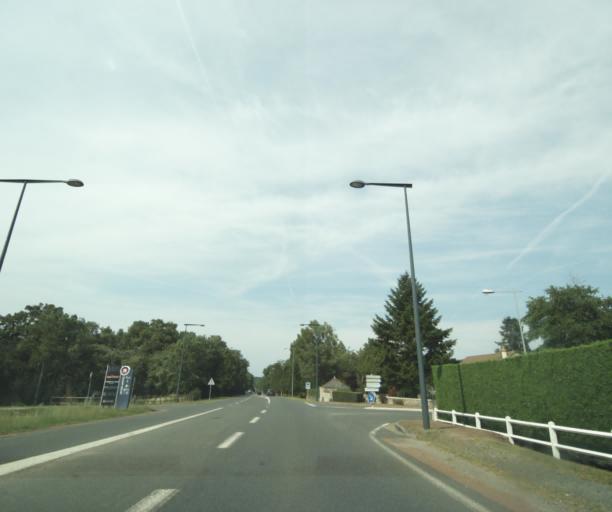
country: FR
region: Centre
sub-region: Departement d'Indre-et-Loire
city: Montbazon
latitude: 47.2792
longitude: 0.7109
